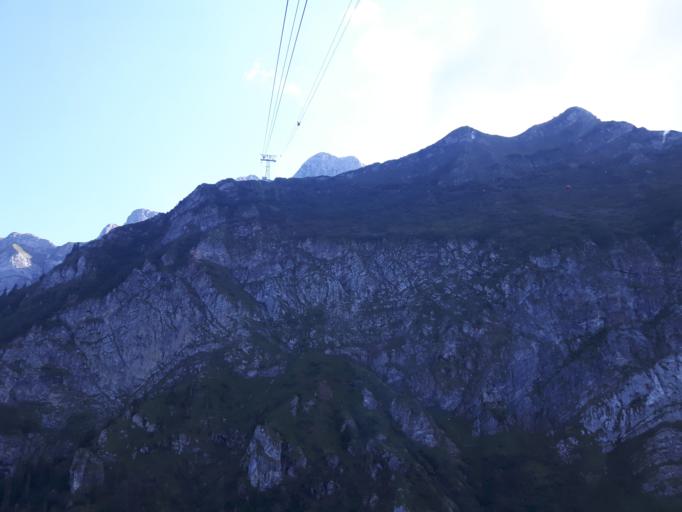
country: CH
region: Obwalden
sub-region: Obwalden
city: Alpnach
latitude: 46.9875
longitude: 8.2526
